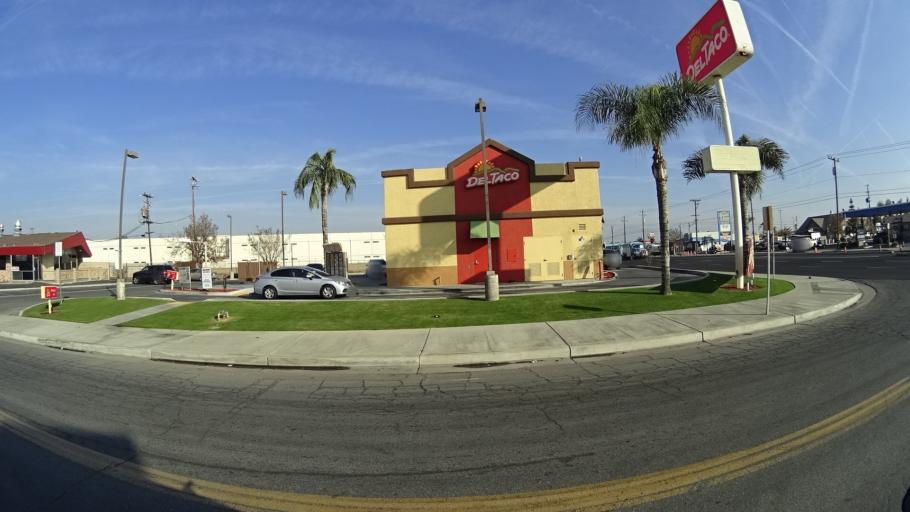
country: US
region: California
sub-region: Kern County
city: Bakersfield
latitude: 35.3179
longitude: -119.0324
